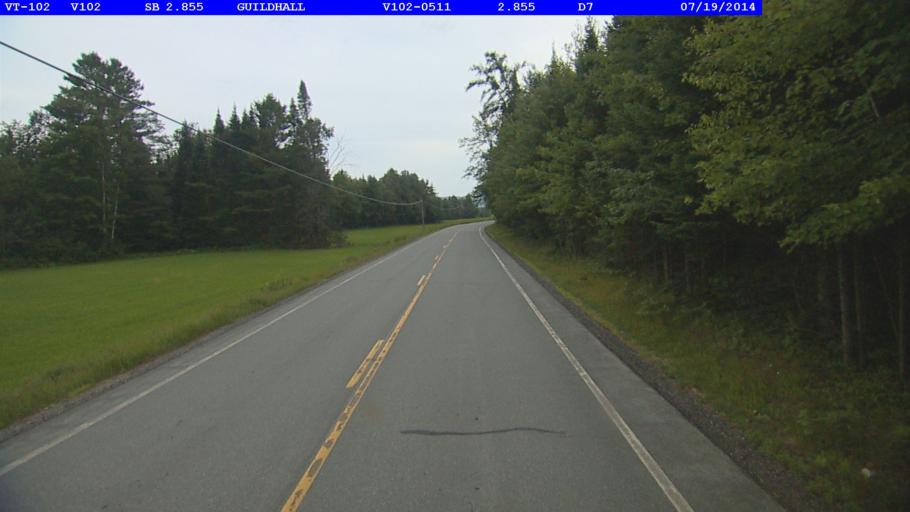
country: US
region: New Hampshire
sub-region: Coos County
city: Northumberland
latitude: 44.5343
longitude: -71.5855
